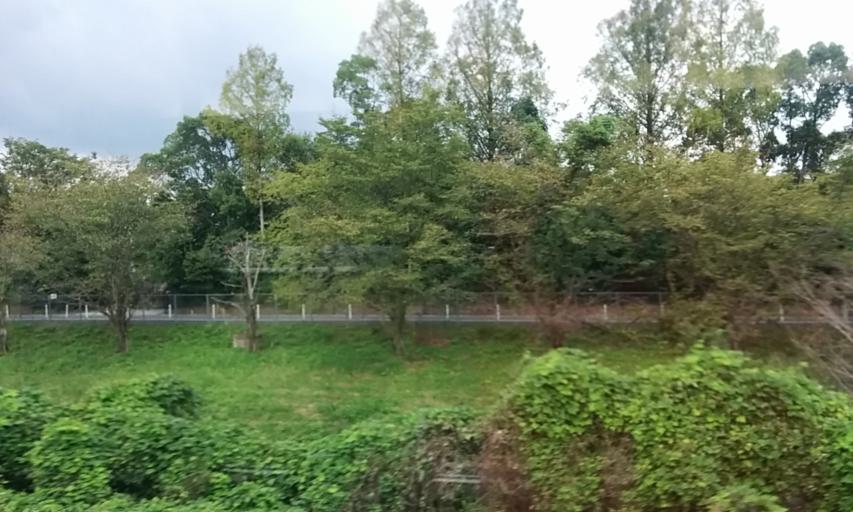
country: JP
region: Nara
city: Tawaramoto
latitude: 34.5943
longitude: 135.7847
